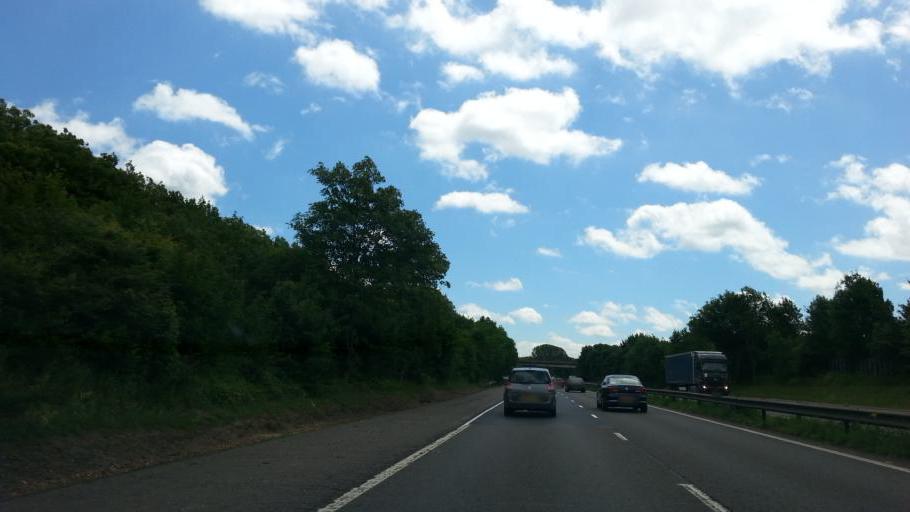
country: GB
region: England
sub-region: Cambridgeshire
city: Grantchester
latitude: 52.1740
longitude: 0.0838
